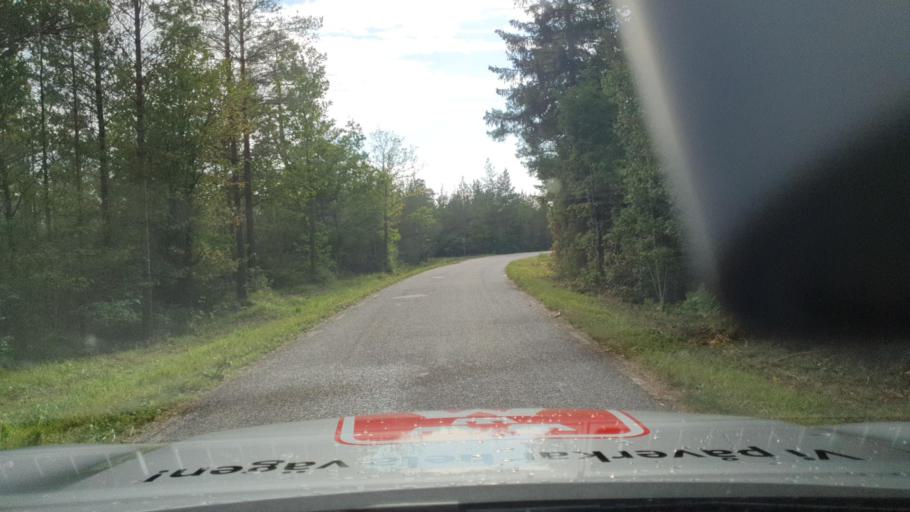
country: SE
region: Gotland
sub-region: Gotland
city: Slite
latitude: 57.5793
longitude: 18.6837
